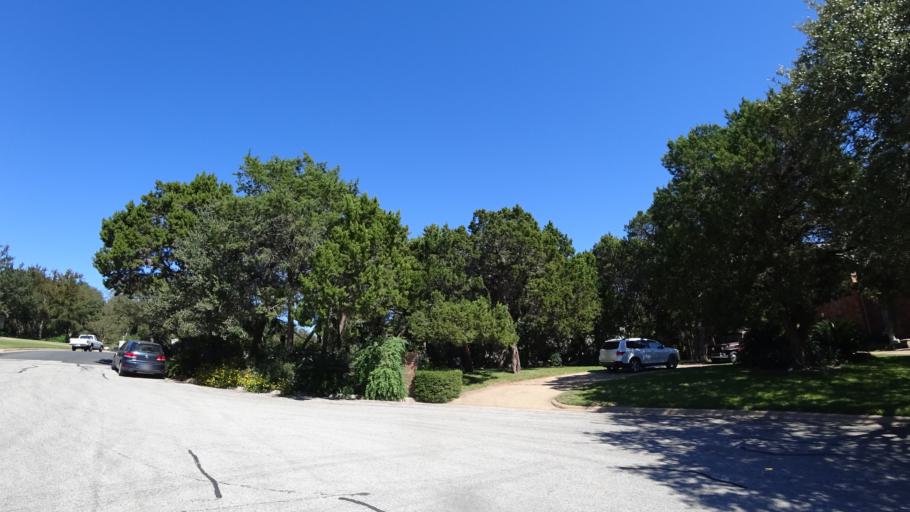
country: US
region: Texas
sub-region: Travis County
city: West Lake Hills
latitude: 30.3239
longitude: -97.7880
